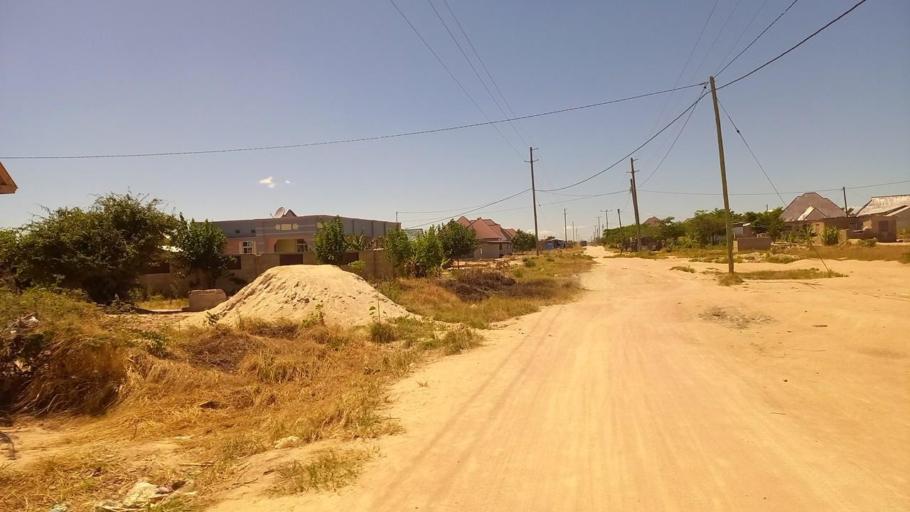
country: TZ
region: Dodoma
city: Dodoma
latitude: -6.1320
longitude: 35.7214
